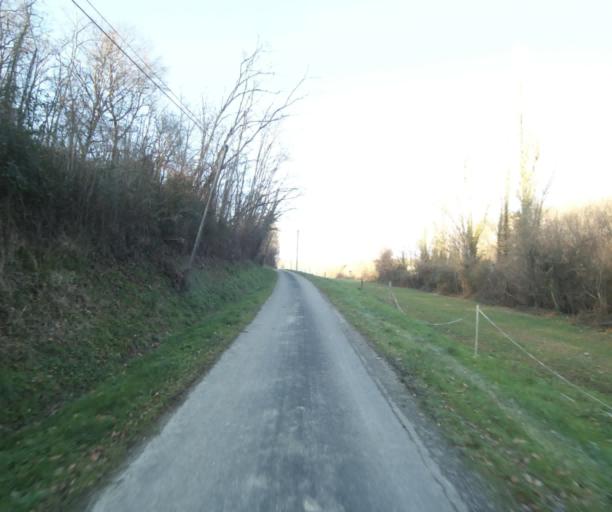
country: FR
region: Midi-Pyrenees
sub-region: Departement du Tarn-et-Garonne
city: Moissac
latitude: 44.1322
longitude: 1.1314
